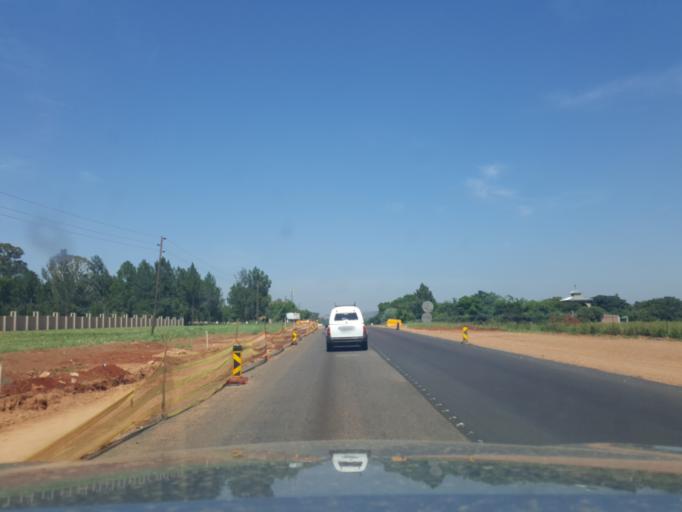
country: ZA
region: Gauteng
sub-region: City of Tshwane Metropolitan Municipality
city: Pretoria
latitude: -25.6756
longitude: 28.3316
